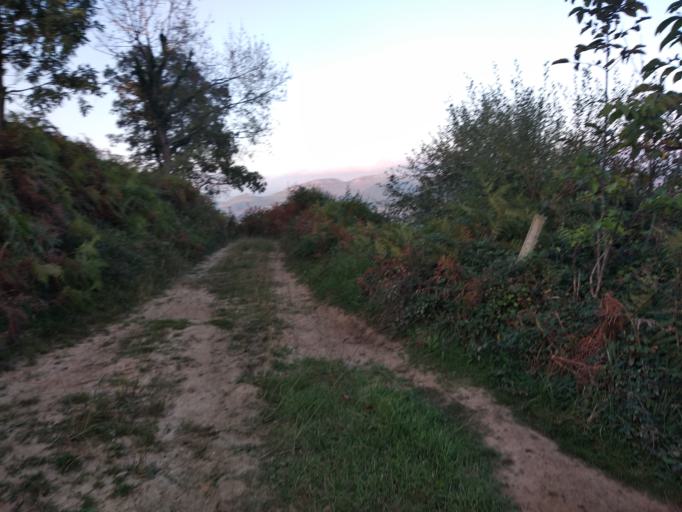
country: ES
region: Cantabria
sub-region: Provincia de Cantabria
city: Entrambasaguas
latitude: 43.3246
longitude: -3.6775
